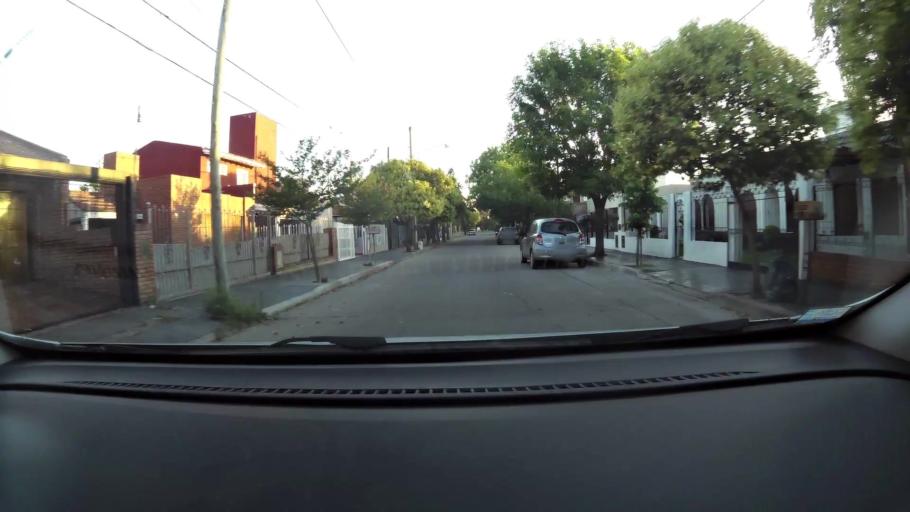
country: AR
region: Cordoba
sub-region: Departamento de Capital
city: Cordoba
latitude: -31.3767
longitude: -64.2171
